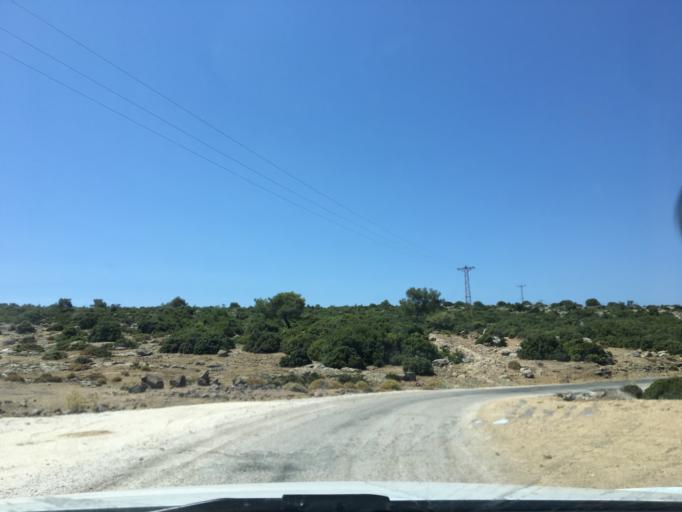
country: TR
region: Canakkale
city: Gulpinar
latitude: 39.4990
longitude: 26.1349
